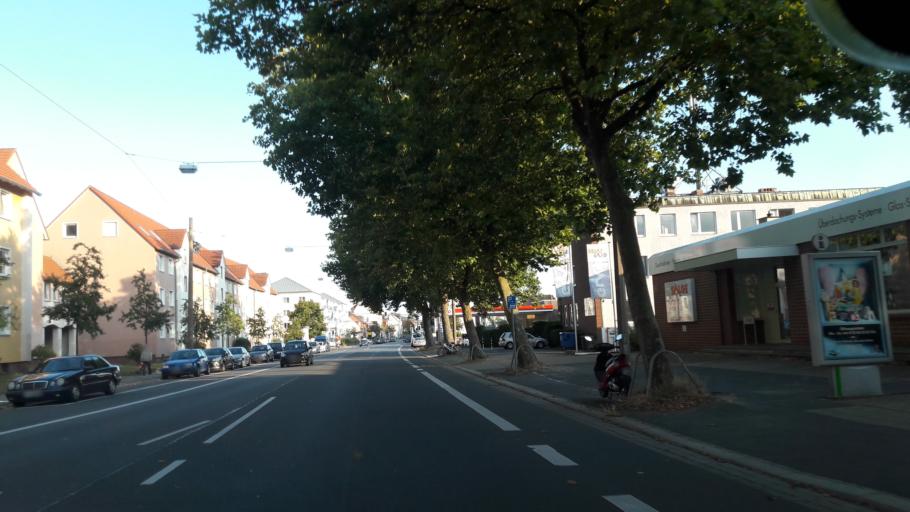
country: DE
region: Lower Saxony
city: Hildesheim
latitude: 52.1667
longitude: 9.9407
